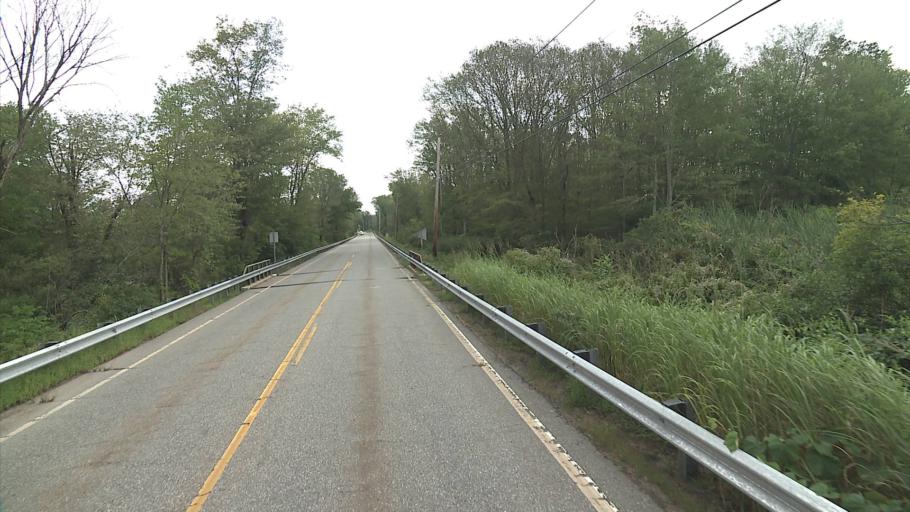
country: US
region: Connecticut
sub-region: New London County
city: Colchester
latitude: 41.4618
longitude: -72.2926
